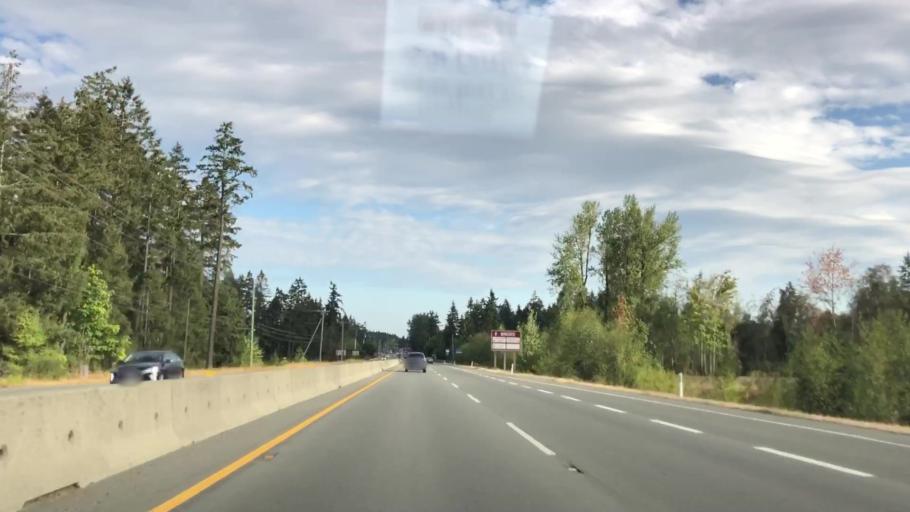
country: CA
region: British Columbia
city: Duncan
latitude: 48.7359
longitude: -123.6487
